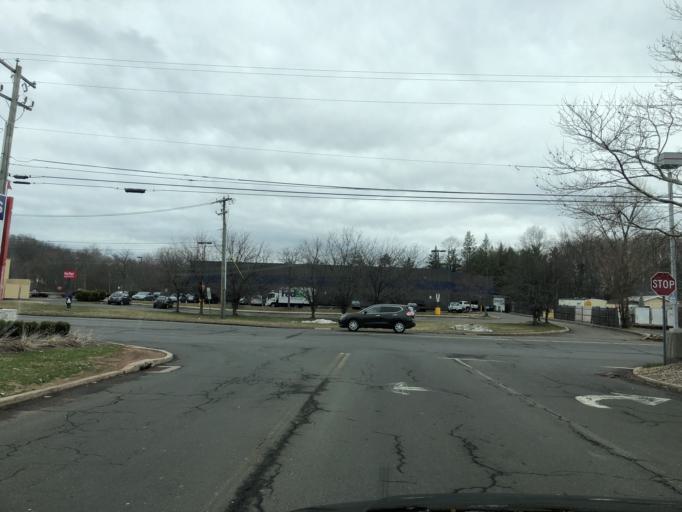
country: US
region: Connecticut
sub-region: Hartford County
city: Kensington
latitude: 41.6495
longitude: -72.7309
